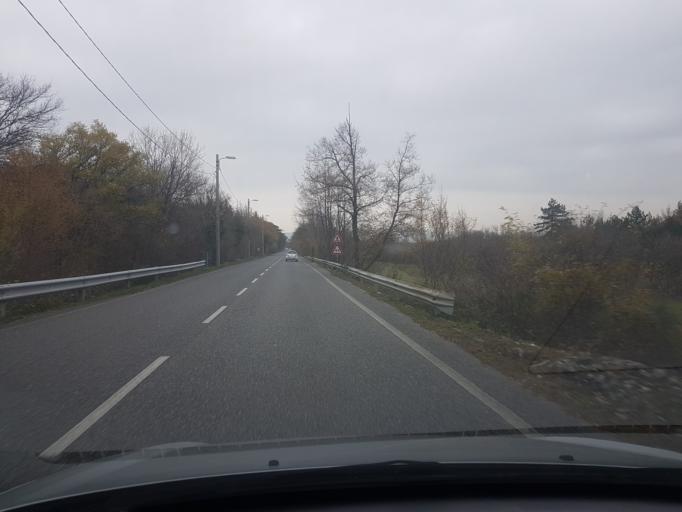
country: IT
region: Friuli Venezia Giulia
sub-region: Provincia di Trieste
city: Santa Croce
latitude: 45.7410
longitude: 13.6847
